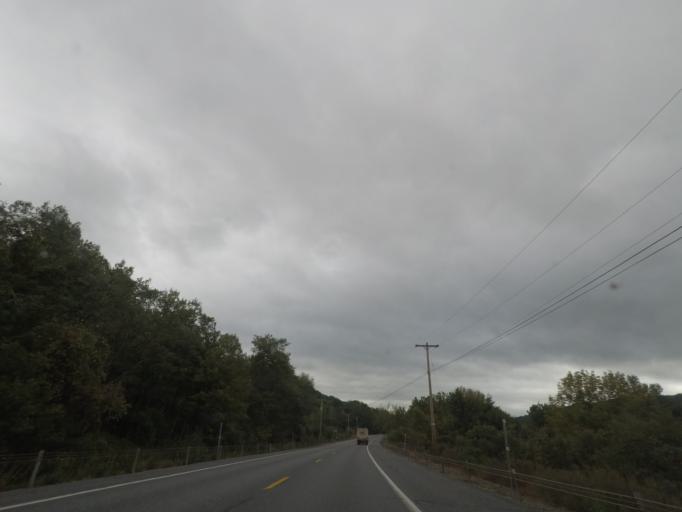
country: US
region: New York
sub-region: Rensselaer County
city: Hoosick Falls
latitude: 42.9446
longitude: -73.3686
